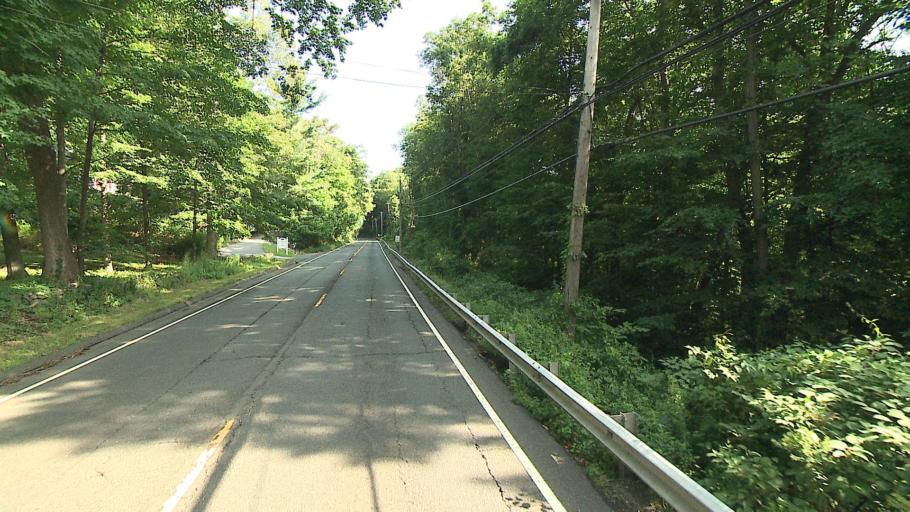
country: US
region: Connecticut
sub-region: Fairfield County
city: Georgetown
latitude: 41.2473
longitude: -73.4343
